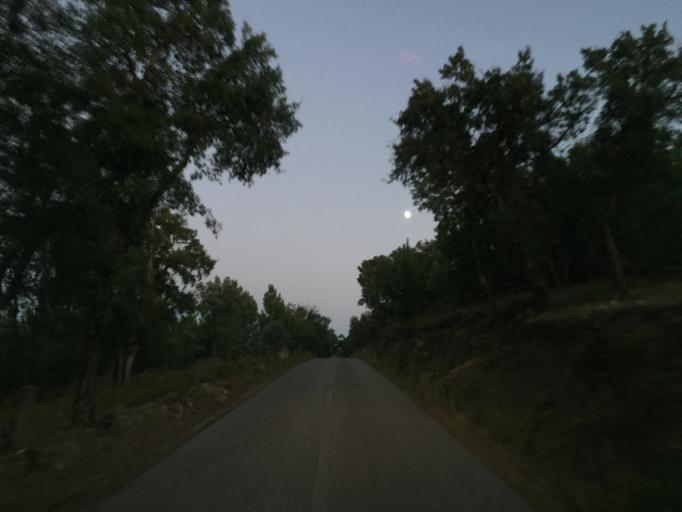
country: PT
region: Portalegre
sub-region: Castelo de Vide
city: Castelo de Vide
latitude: 39.4082
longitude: -7.4634
